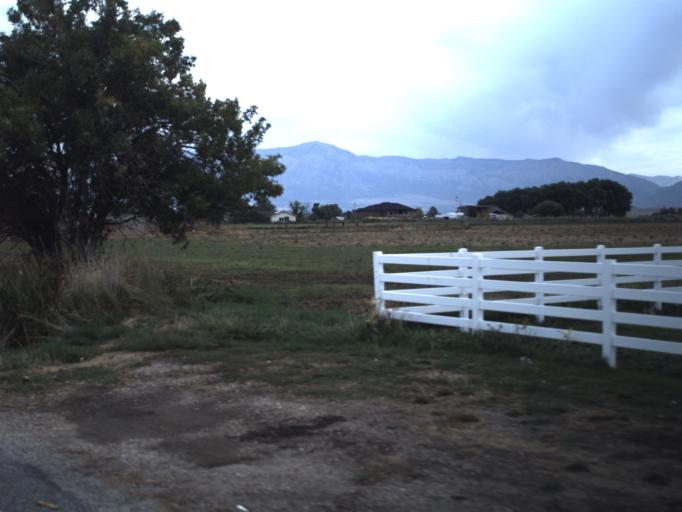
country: US
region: Utah
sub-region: Weber County
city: West Haven
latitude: 41.2242
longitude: -112.0928
